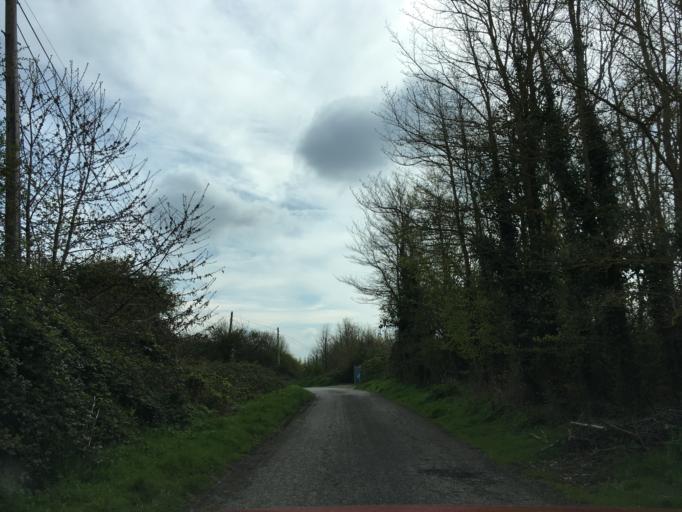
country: GB
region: England
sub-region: South Gloucestershire
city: Almondsbury
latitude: 51.5166
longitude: -2.5966
